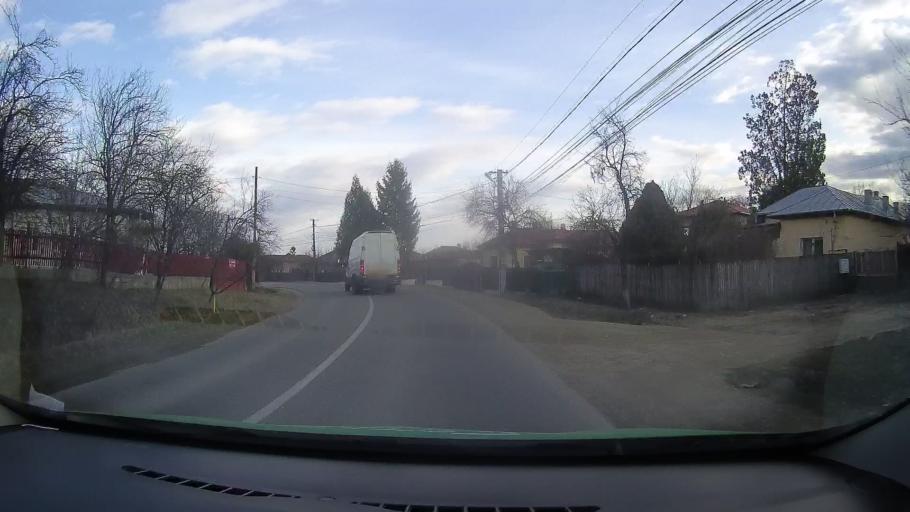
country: RO
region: Dambovita
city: Razvad
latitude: 44.9341
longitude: 25.5401
